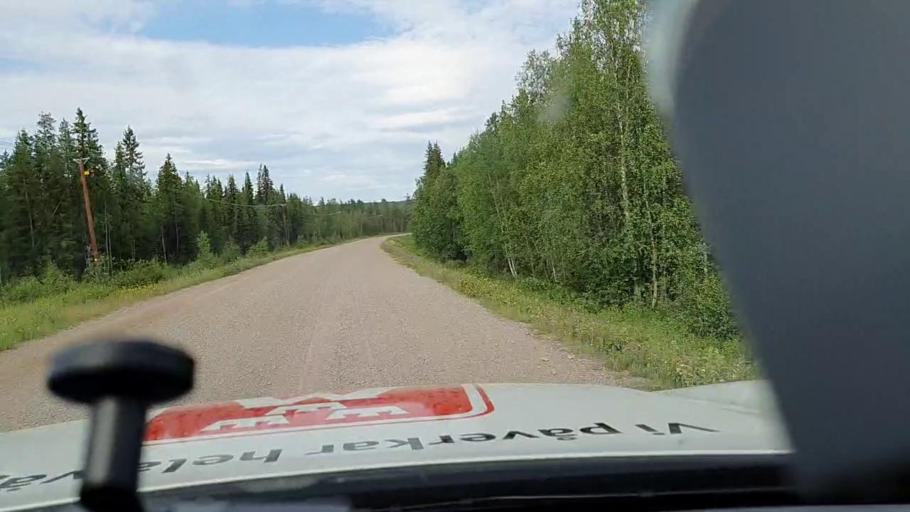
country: SE
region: Norrbotten
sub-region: Alvsbyns Kommun
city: AElvsbyn
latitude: 66.1165
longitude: 20.9757
